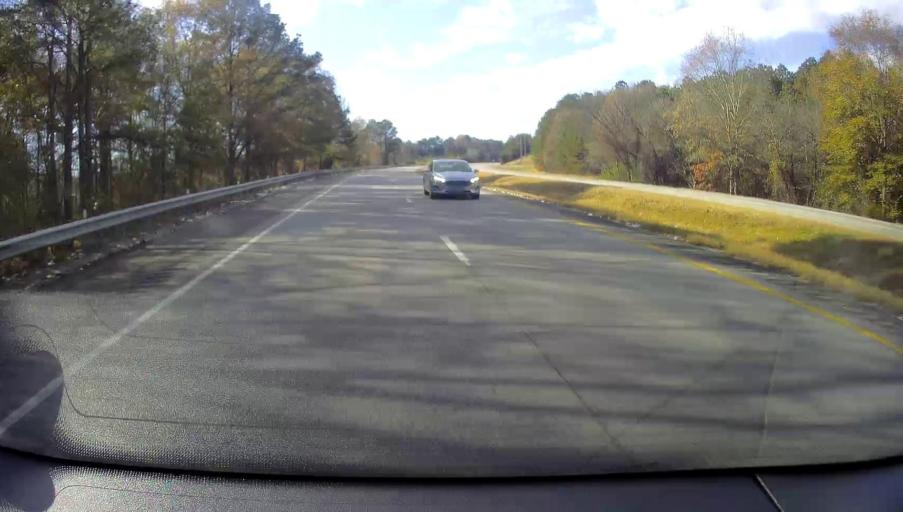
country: US
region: Mississippi
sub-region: Tishomingo County
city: Iuka
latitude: 34.7588
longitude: -88.0893
